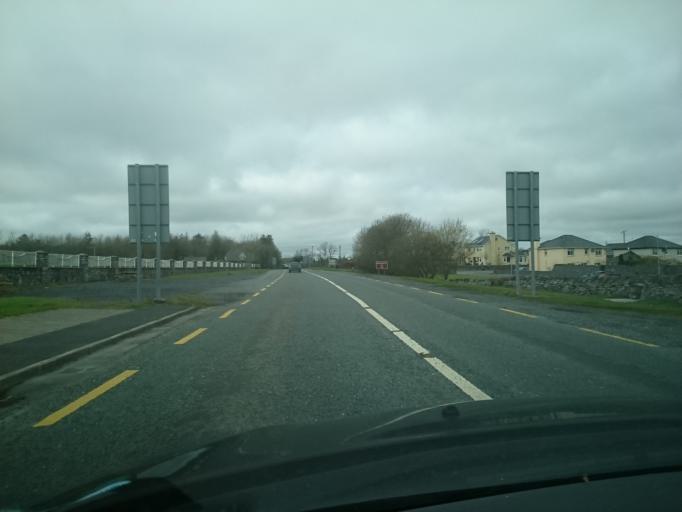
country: IE
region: Connaught
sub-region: Maigh Eo
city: Kiltamagh
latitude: 53.8096
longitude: -9.1380
